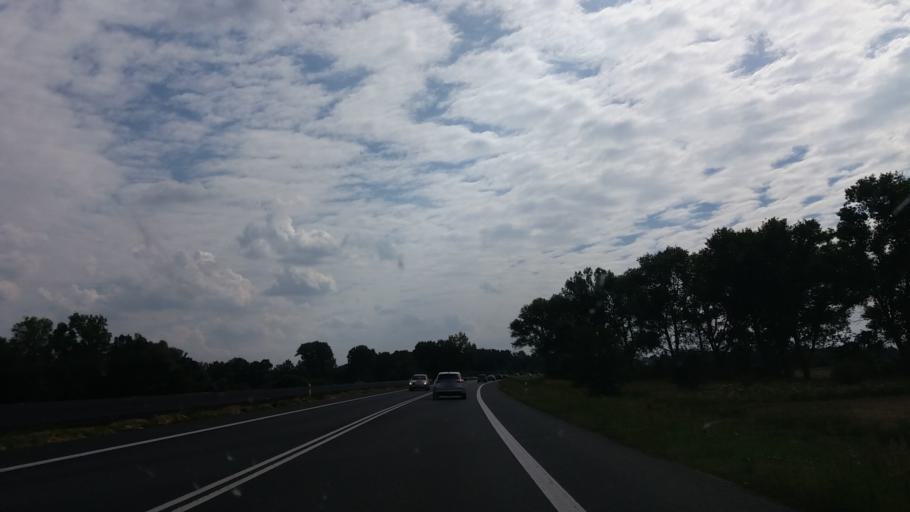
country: PL
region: Lubusz
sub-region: Powiat zielonogorski
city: Sulechow
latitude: 52.0219
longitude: 15.6295
